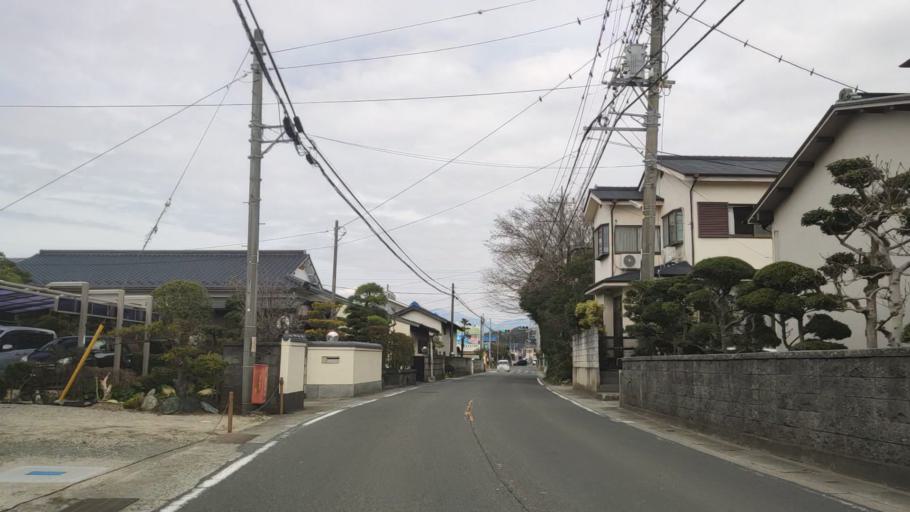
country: JP
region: Kanagawa
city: Ninomiya
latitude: 35.2954
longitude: 139.2329
